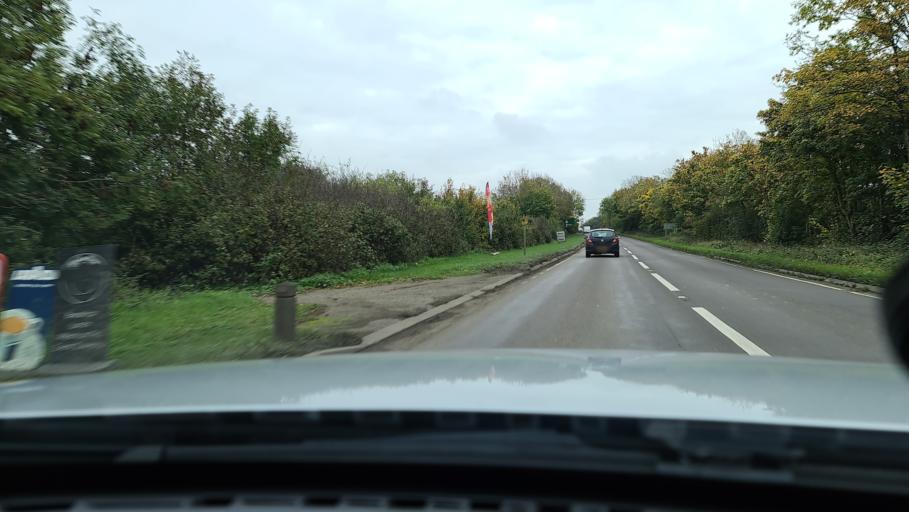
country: GB
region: England
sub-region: Oxfordshire
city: Bicester
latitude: 51.8793
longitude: -1.1200
